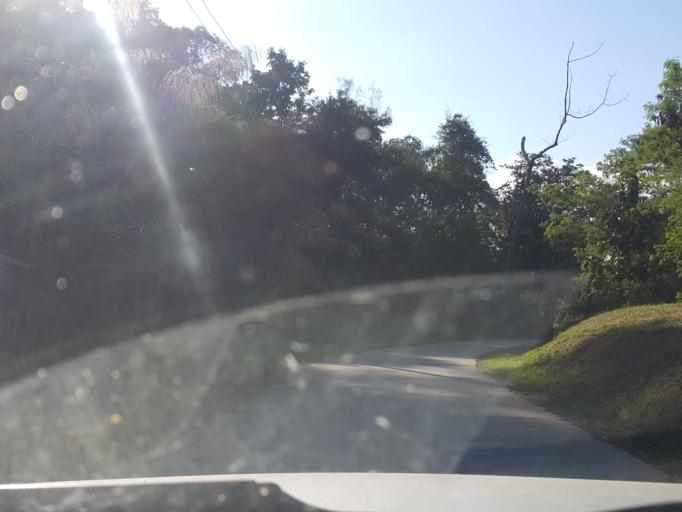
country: TH
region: Mae Hong Son
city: Mae Hi
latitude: 19.3074
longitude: 98.4716
